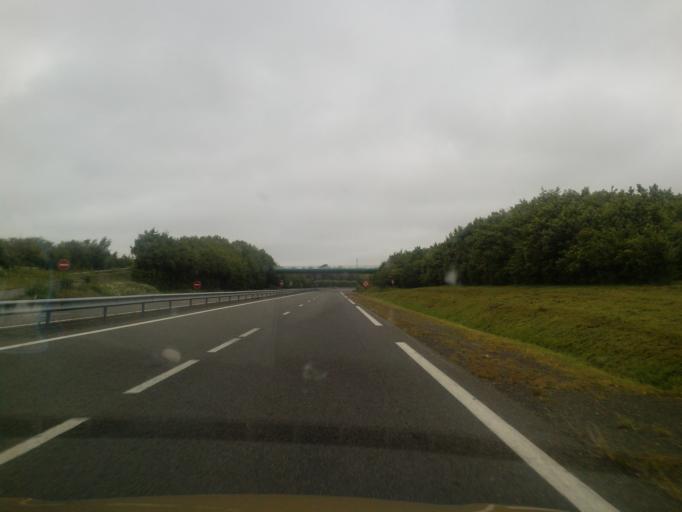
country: FR
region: Brittany
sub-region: Departement d'Ille-et-Vilaine
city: Chasne-sur-Illet
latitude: 48.2760
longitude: -1.5997
